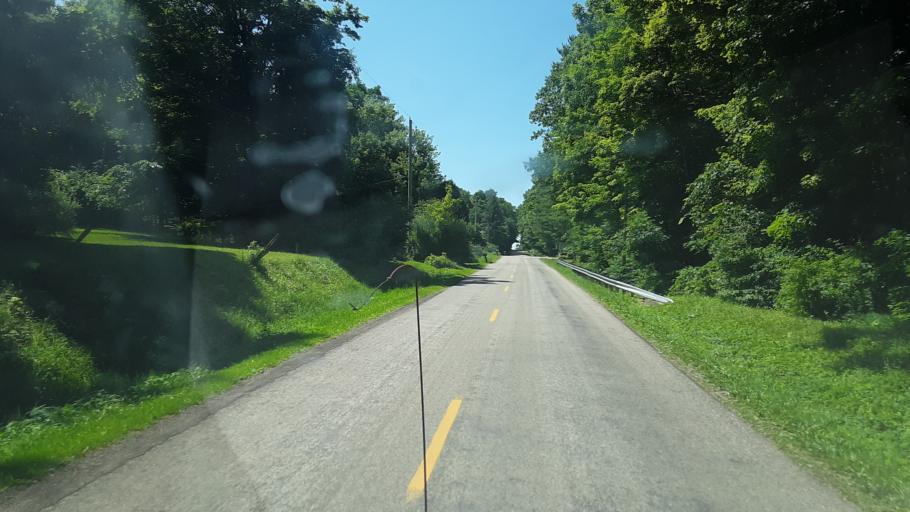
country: US
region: Ohio
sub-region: Ashland County
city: Ashland
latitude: 40.7807
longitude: -82.3258
